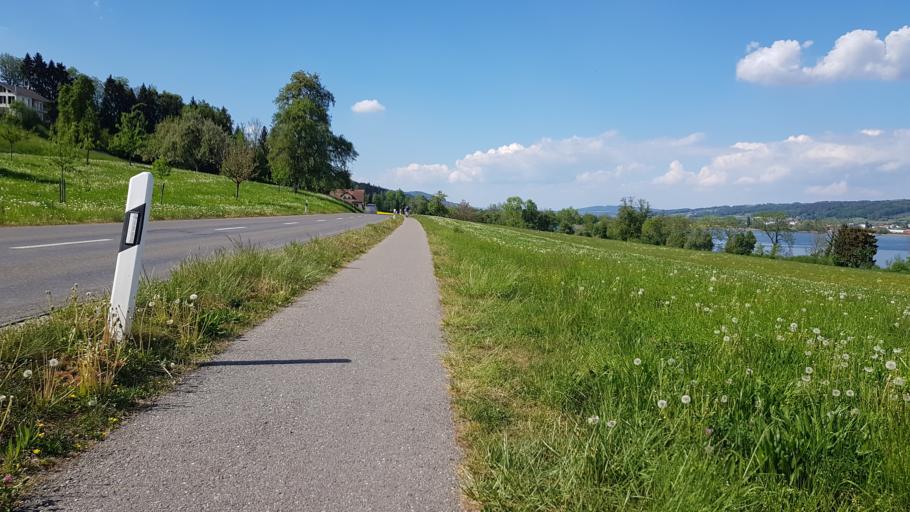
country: CH
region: Lucerne
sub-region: Hochdorf District
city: Hitzkirch
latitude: 47.2001
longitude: 8.2482
